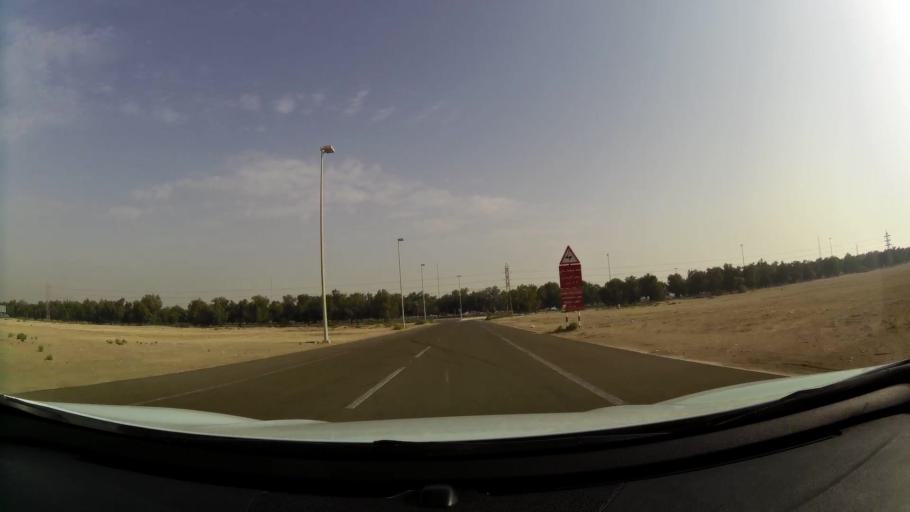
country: AE
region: Abu Dhabi
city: Abu Dhabi
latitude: 24.2635
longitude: 54.6750
